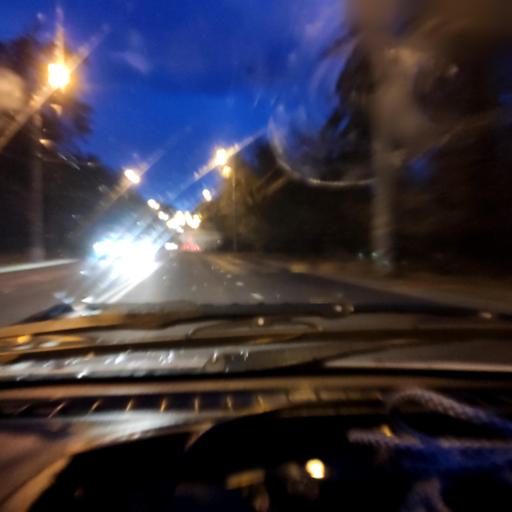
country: RU
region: Samara
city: Zhigulevsk
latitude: 53.5027
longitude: 49.4635
